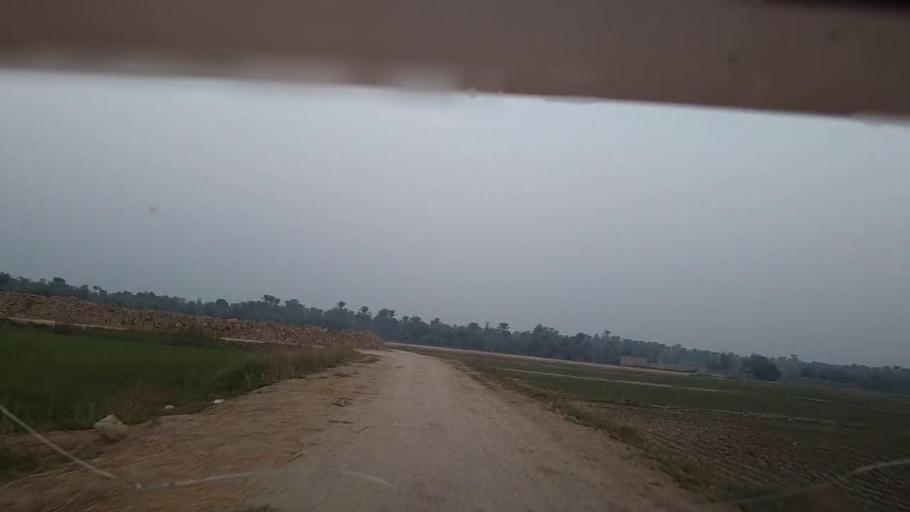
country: PK
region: Sindh
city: Khairpur
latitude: 27.5775
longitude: 68.7353
